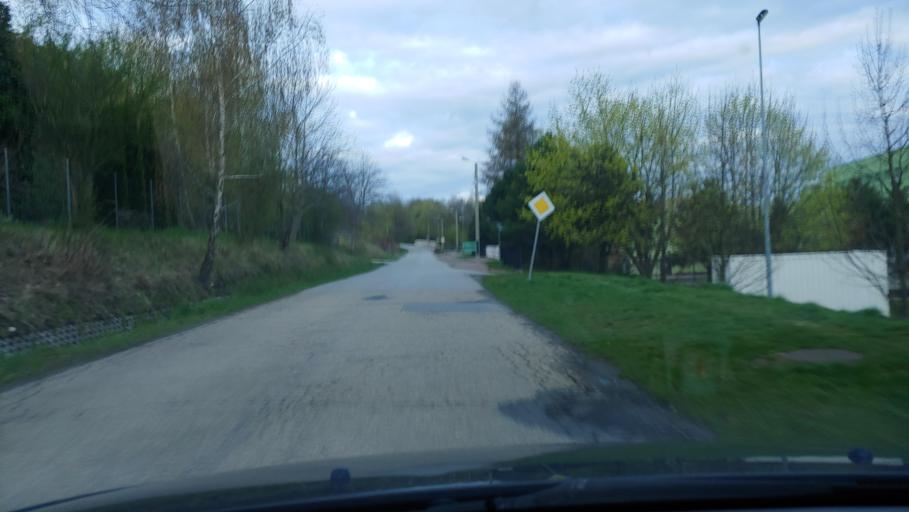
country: PL
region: Lesser Poland Voivodeship
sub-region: Powiat krakowski
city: Bolechowice
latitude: 50.1527
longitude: 19.7715
